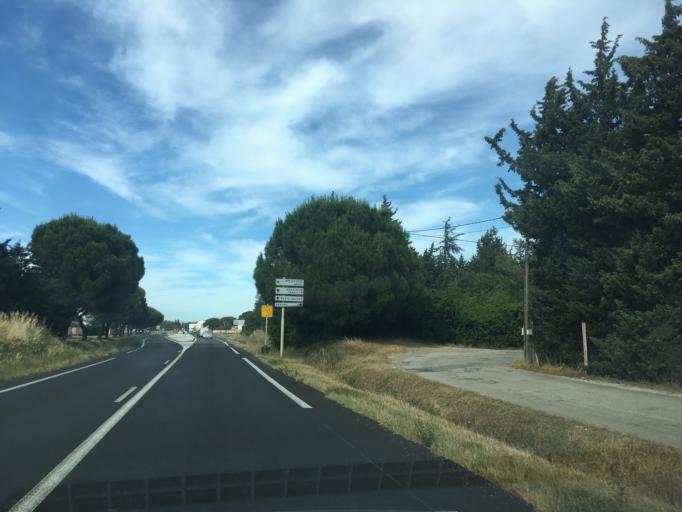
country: FR
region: Languedoc-Roussillon
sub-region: Departement du Gard
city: Garons
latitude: 43.7746
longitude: 4.4255
